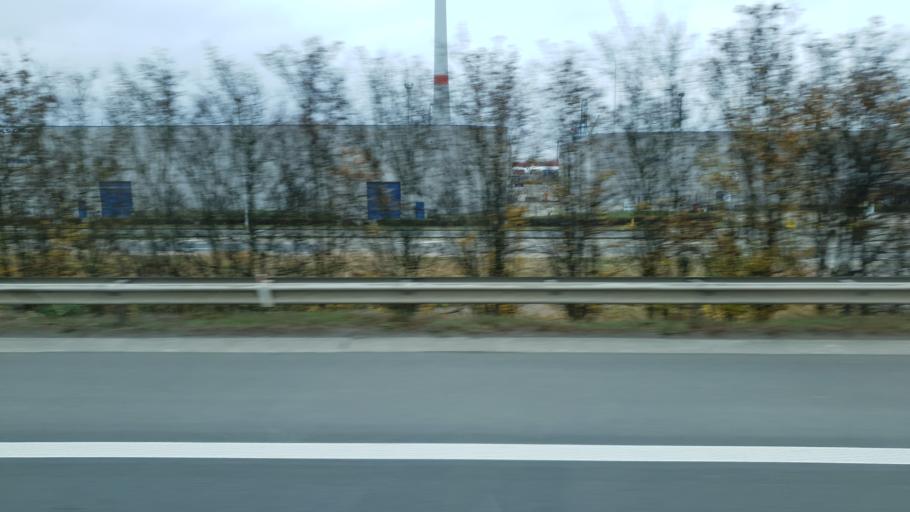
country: BE
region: Flanders
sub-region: Provincie Antwerpen
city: Stabroek
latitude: 51.3165
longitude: 4.3439
